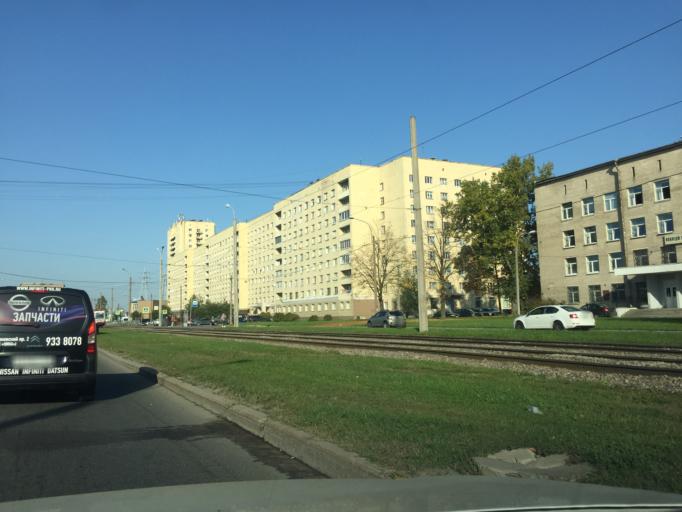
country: RU
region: St.-Petersburg
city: Grazhdanka
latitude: 60.0113
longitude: 30.4344
